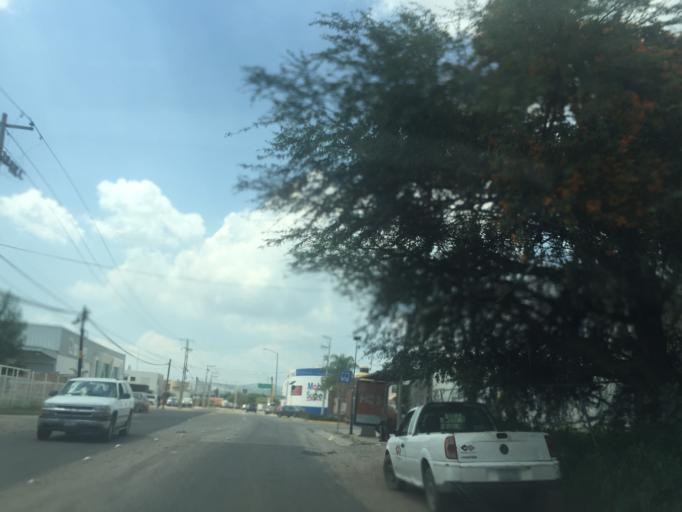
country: MX
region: Guanajuato
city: Leon
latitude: 21.1690
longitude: -101.6778
